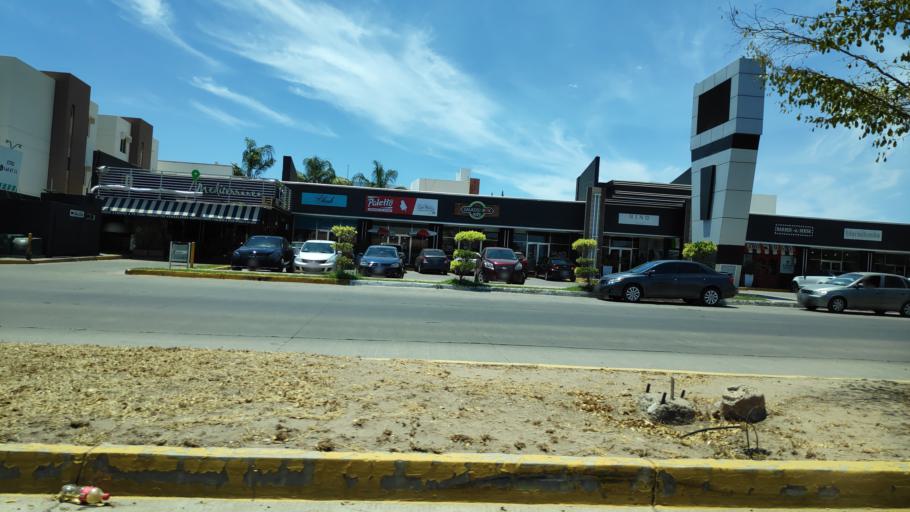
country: MX
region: Sinaloa
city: Culiacan
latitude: 24.8281
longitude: -107.3996
